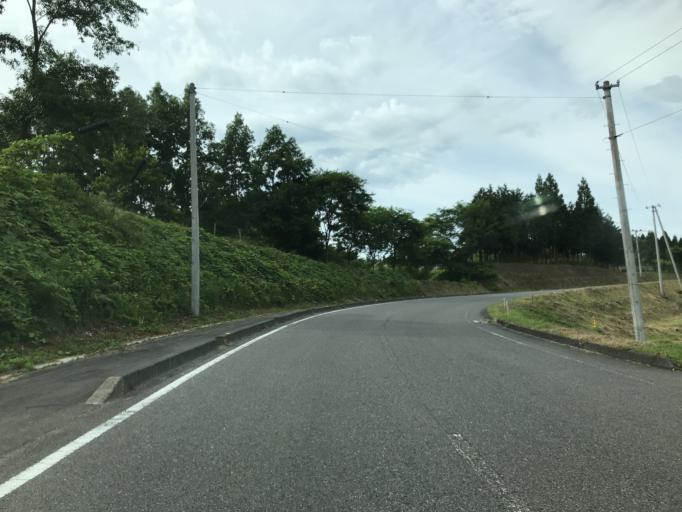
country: JP
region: Fukushima
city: Funehikimachi-funehiki
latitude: 37.5074
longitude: 140.5599
